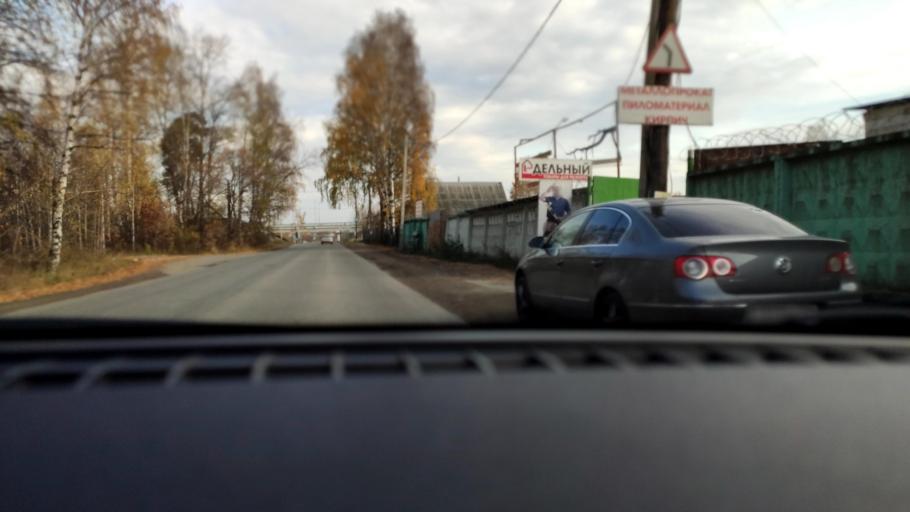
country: RU
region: Perm
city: Kondratovo
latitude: 58.0422
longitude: 56.0264
